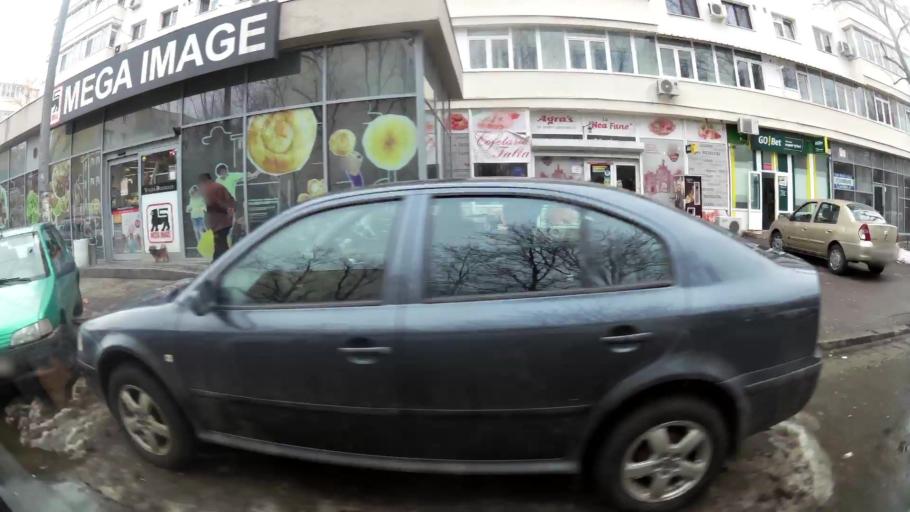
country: RO
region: Ilfov
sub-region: Comuna Popesti-Leordeni
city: Popesti-Leordeni
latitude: 44.4062
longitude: 26.1751
